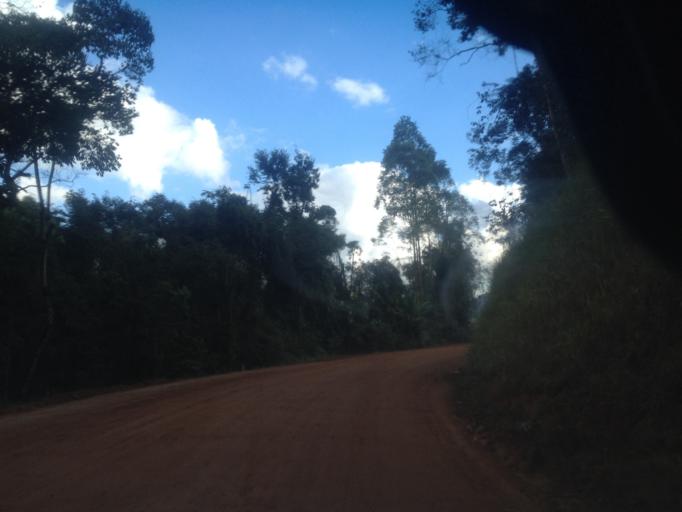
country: BR
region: Rio de Janeiro
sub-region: Quatis
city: Quatis
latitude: -22.2202
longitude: -44.2496
